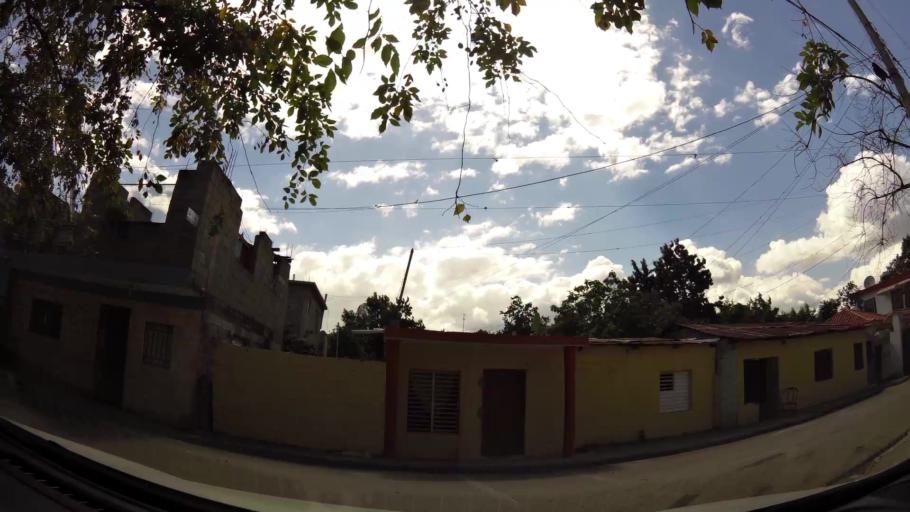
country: DO
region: San Cristobal
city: San Cristobal
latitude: 18.4231
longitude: -70.1036
